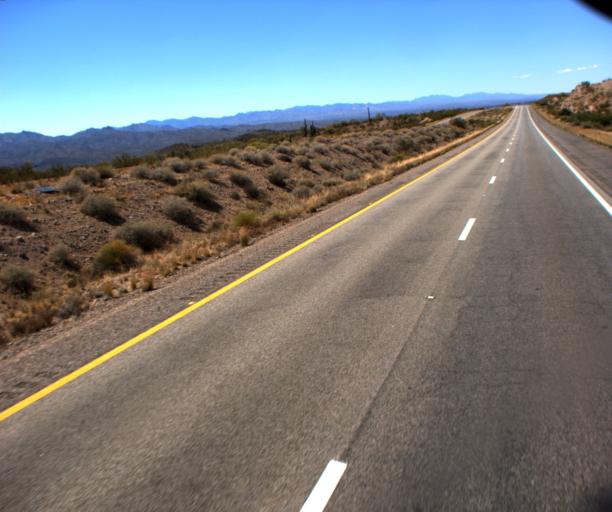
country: US
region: Arizona
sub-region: Yavapai County
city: Bagdad
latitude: 34.6046
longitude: -113.5212
